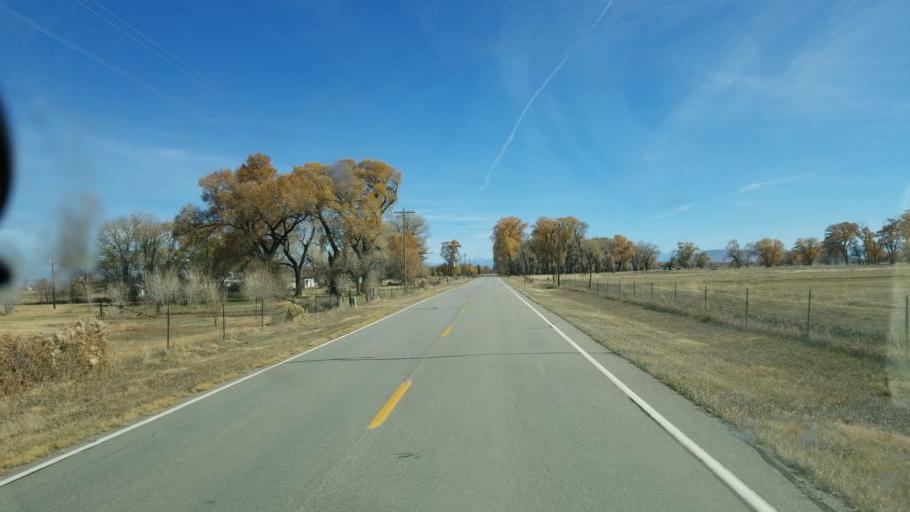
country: US
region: Colorado
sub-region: Conejos County
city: Conejos
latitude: 37.2835
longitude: -106.0827
